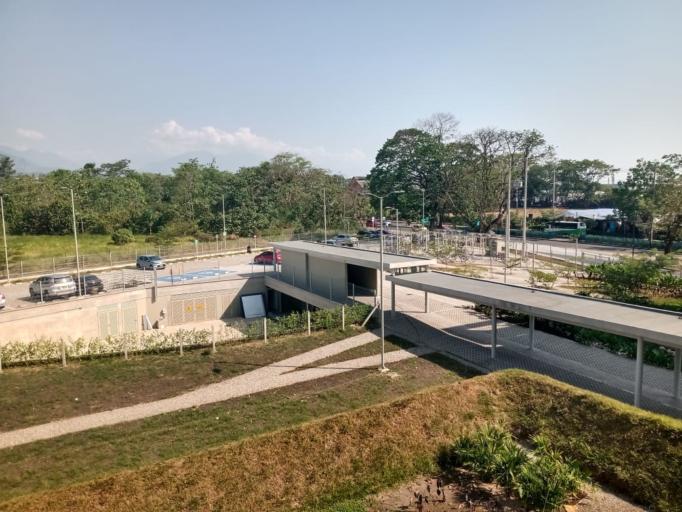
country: CO
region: Meta
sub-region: Villavicencio
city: Villavicencio
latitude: 4.1128
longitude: -73.6344
